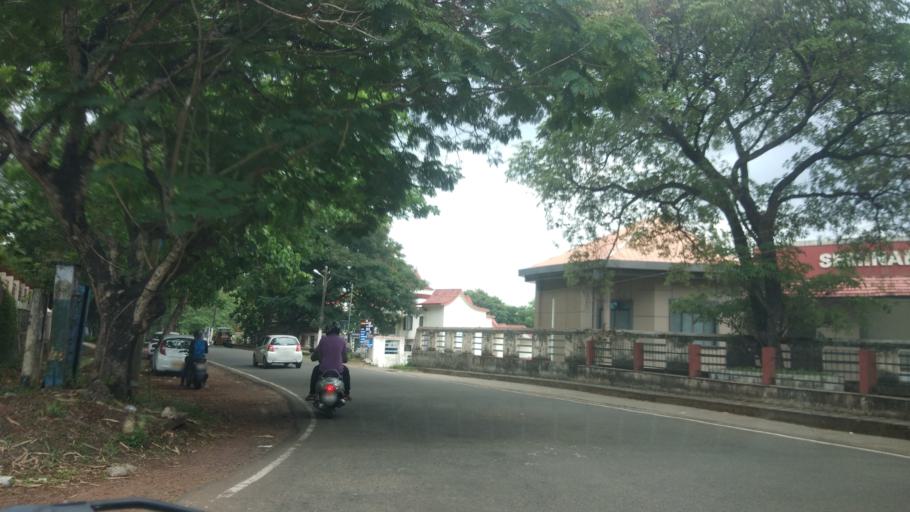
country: IN
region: Kerala
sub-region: Ernakulam
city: Elur
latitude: 10.0442
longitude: 76.3247
